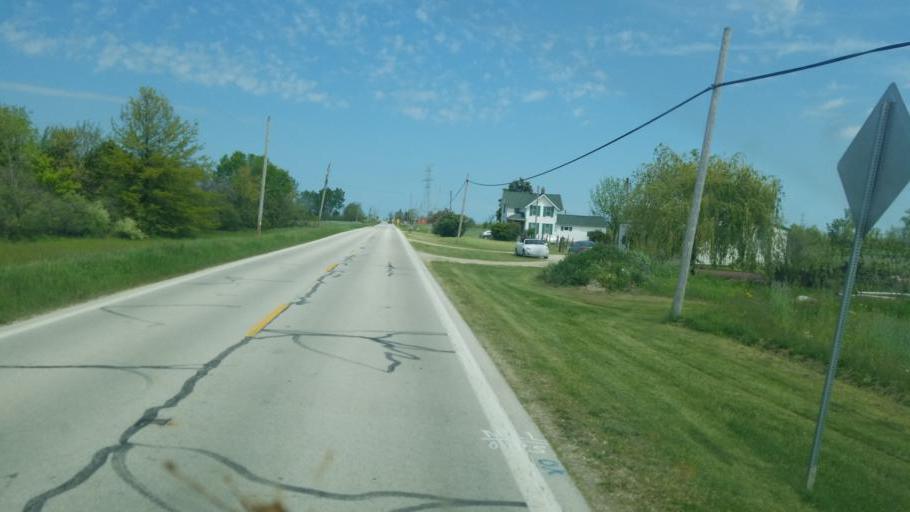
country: US
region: Ohio
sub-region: Ottawa County
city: Oak Harbor
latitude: 41.5858
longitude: -83.1450
